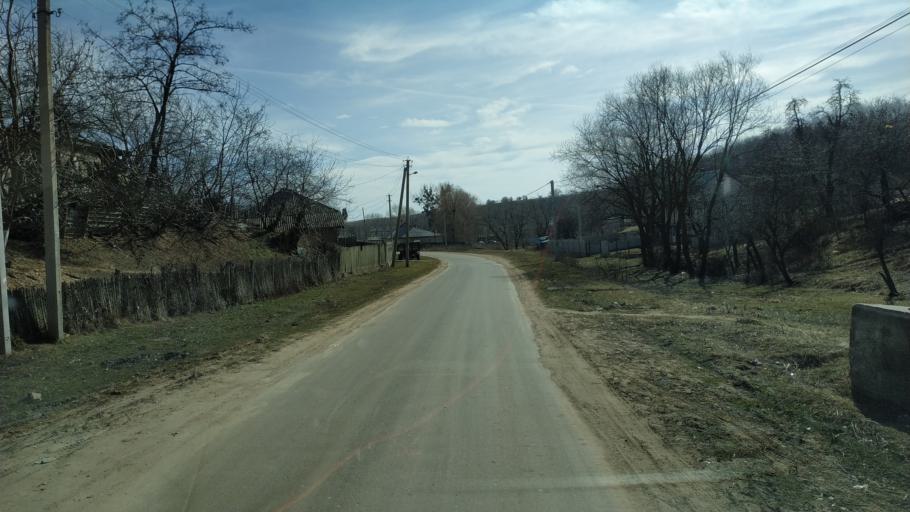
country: MD
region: Nisporeni
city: Nisporeni
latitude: 47.0975
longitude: 28.2944
